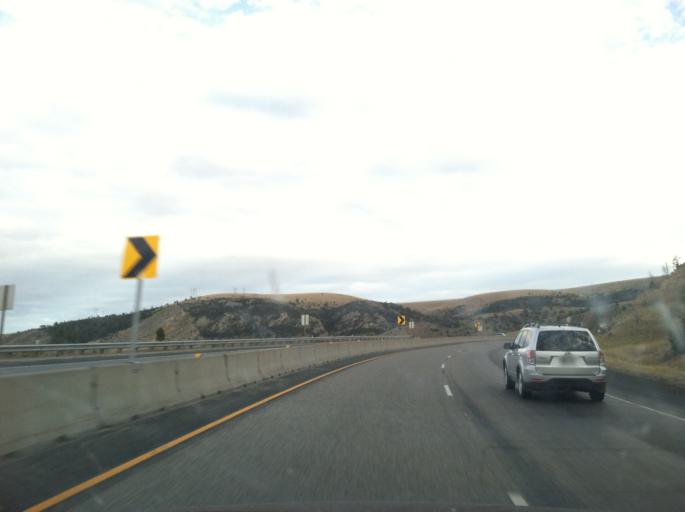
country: US
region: Montana
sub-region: Jefferson County
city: Whitehall
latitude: 45.8802
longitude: -111.8986
